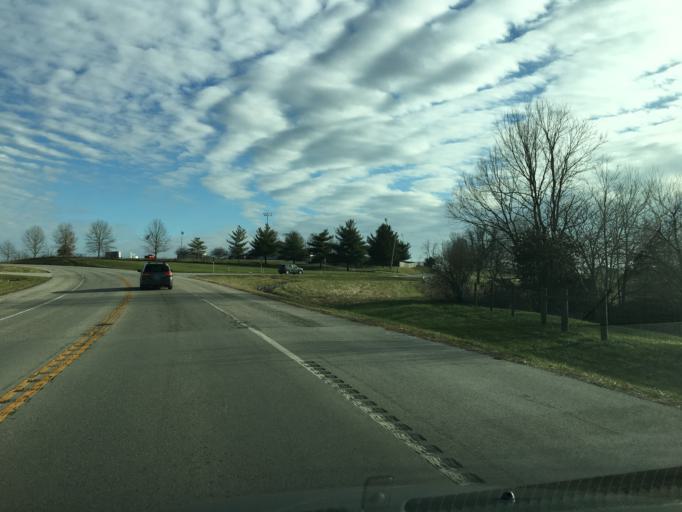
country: US
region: Kentucky
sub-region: Scott County
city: Georgetown
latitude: 38.2396
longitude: -84.5763
